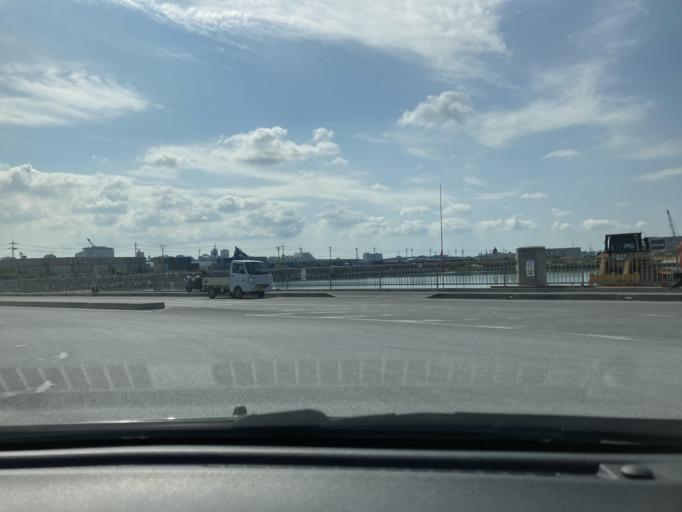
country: JP
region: Okinawa
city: Naha-shi
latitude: 26.2414
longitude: 127.6708
